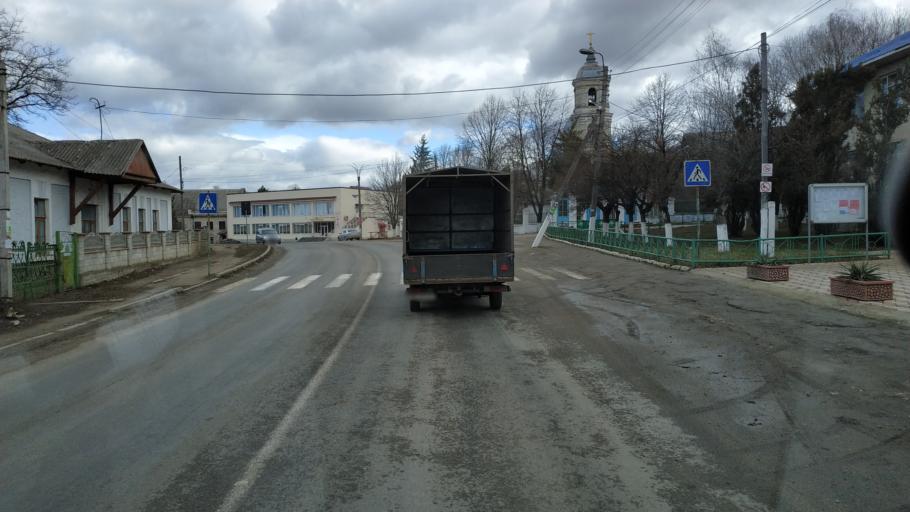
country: MD
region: Stinga Nistrului
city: Bucovat
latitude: 47.1528
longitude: 28.4262
